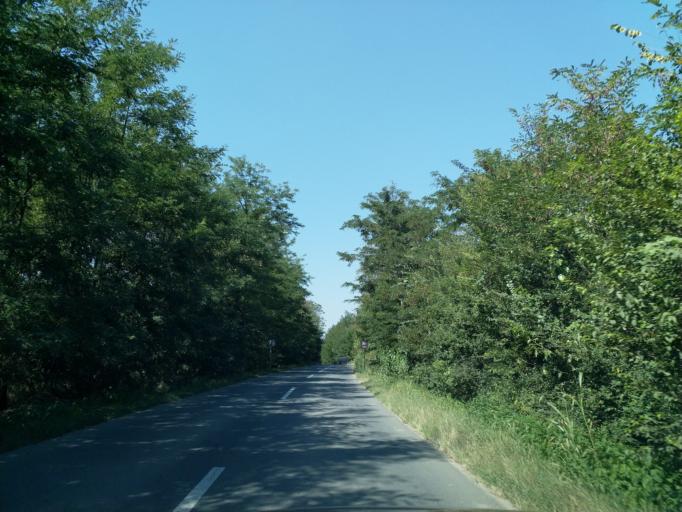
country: RS
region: Central Serbia
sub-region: Rasinski Okrug
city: Trstenik
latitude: 43.6257
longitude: 21.1587
